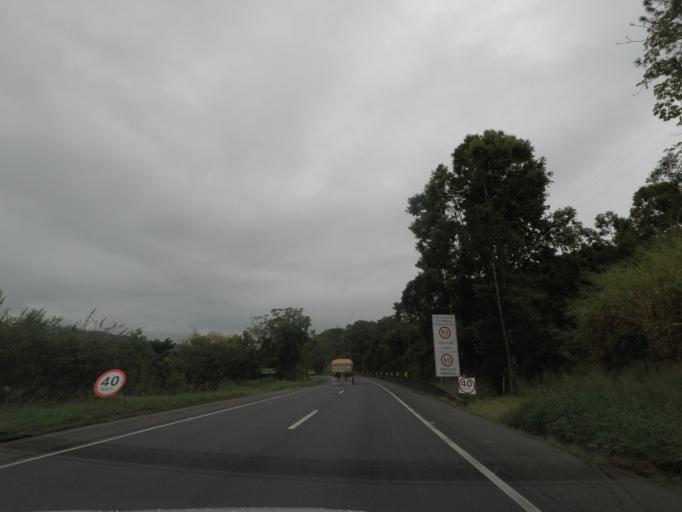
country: BR
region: Sao Paulo
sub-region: Cajati
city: Cajati
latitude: -24.8245
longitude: -48.2091
